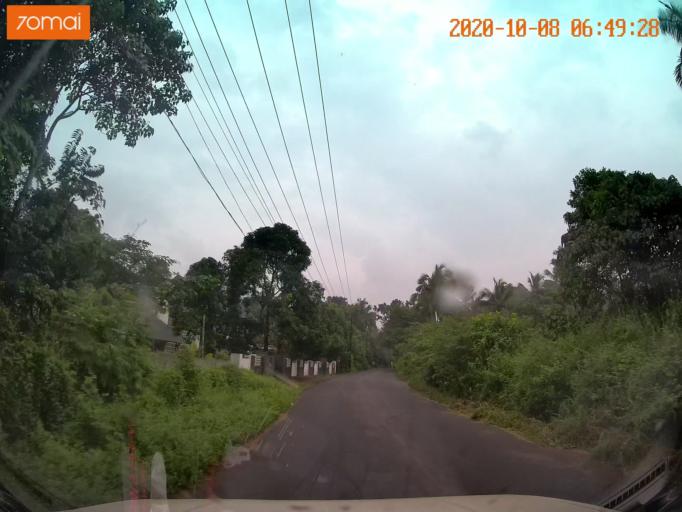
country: IN
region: Kerala
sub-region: Thrissur District
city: Kunnamkulam
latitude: 10.6835
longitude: 76.1026
